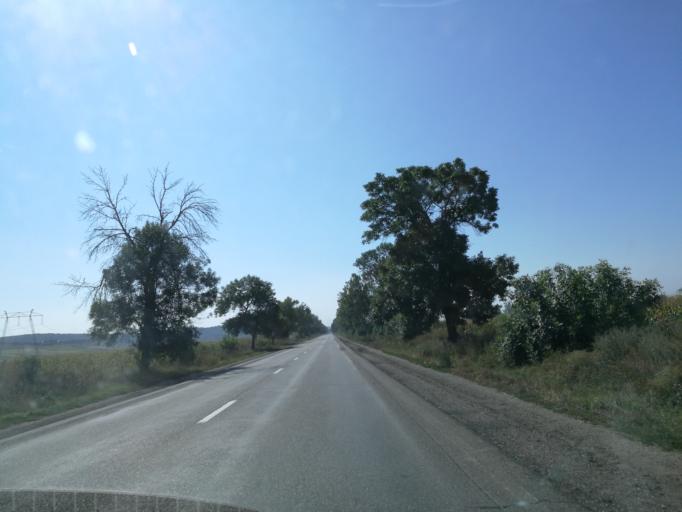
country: RO
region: Iasi
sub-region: Comuna Motca
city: Motca
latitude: 47.2243
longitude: 26.6004
